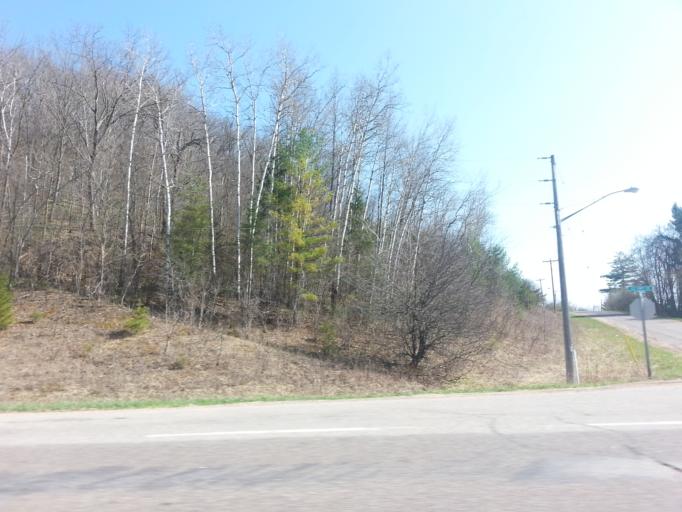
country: US
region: Minnesota
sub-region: Wabasha County
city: Lake City
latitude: 44.6365
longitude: -92.1862
